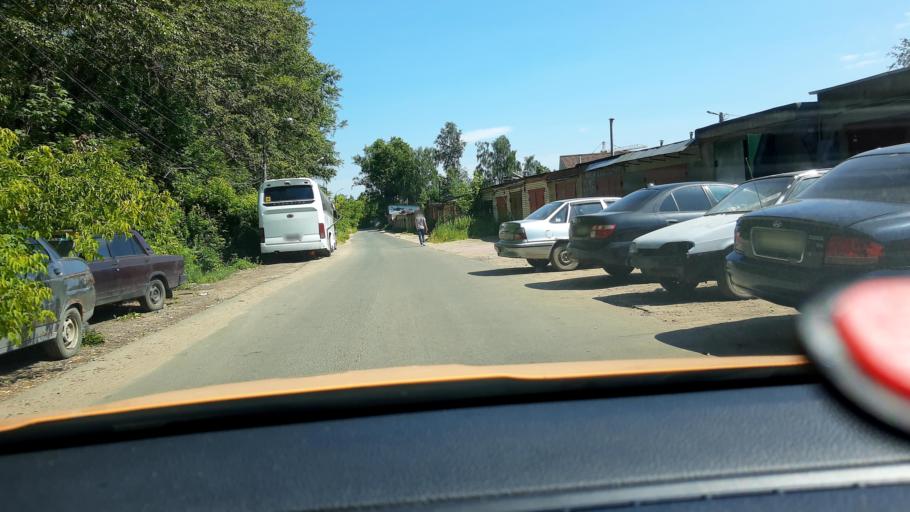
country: RU
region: Moscow
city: Severnyy
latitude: 55.9472
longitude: 37.5285
